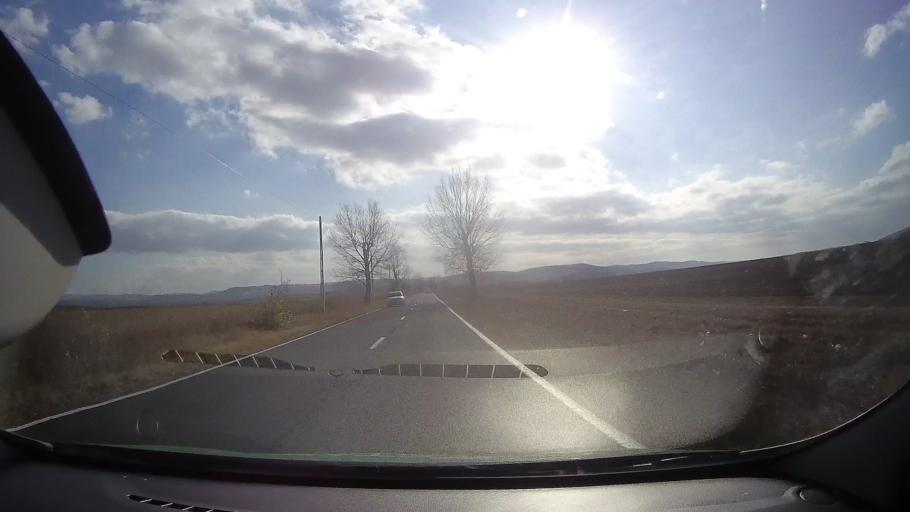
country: RO
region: Tulcea
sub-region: Comuna Nalbant
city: Nicolae Balcescu
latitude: 45.0100
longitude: 28.5986
